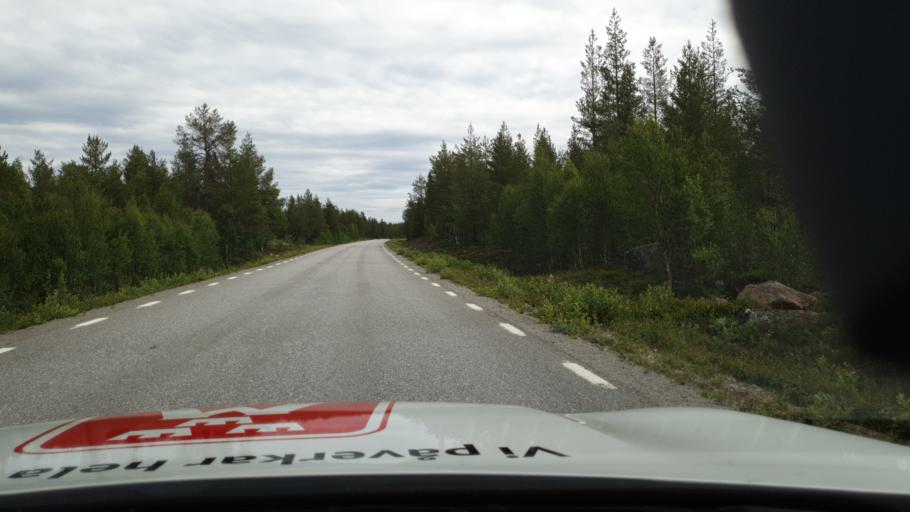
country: SE
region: Vaesterbotten
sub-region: Storumans Kommun
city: Storuman
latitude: 65.5091
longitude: 17.0556
